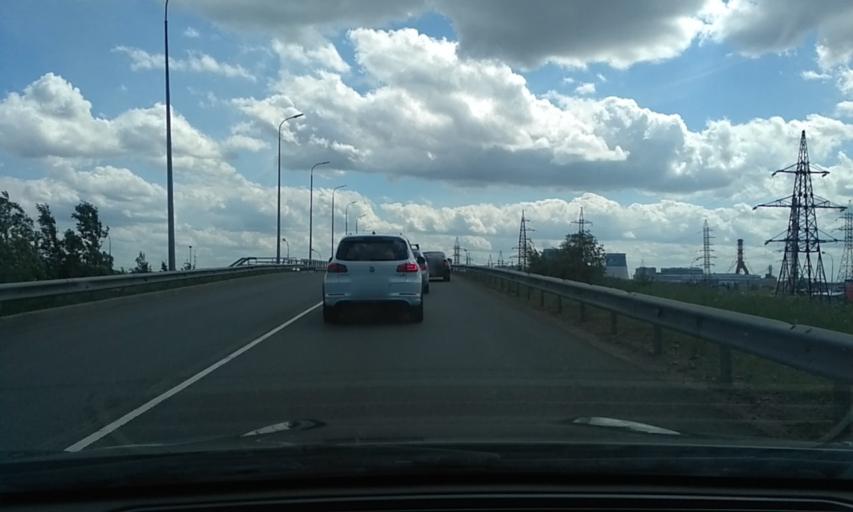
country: RU
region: Leningrad
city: Rybatskoye
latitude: 59.8885
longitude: 30.5050
